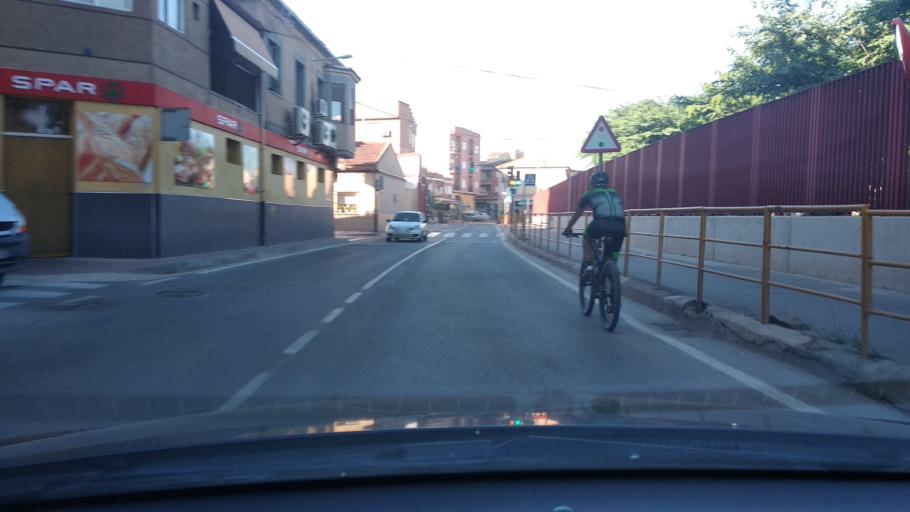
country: ES
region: Murcia
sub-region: Murcia
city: Murcia
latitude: 37.9458
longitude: -1.1085
